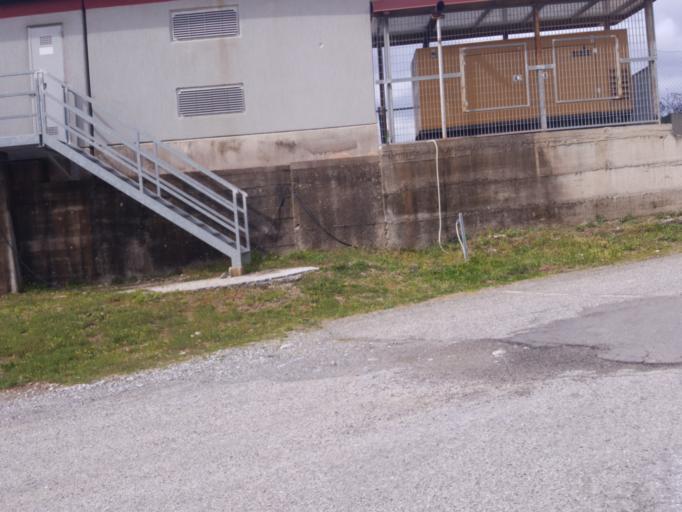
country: IT
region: Calabria
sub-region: Provincia di Cosenza
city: Piane Crati
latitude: 39.2197
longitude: 16.3094
